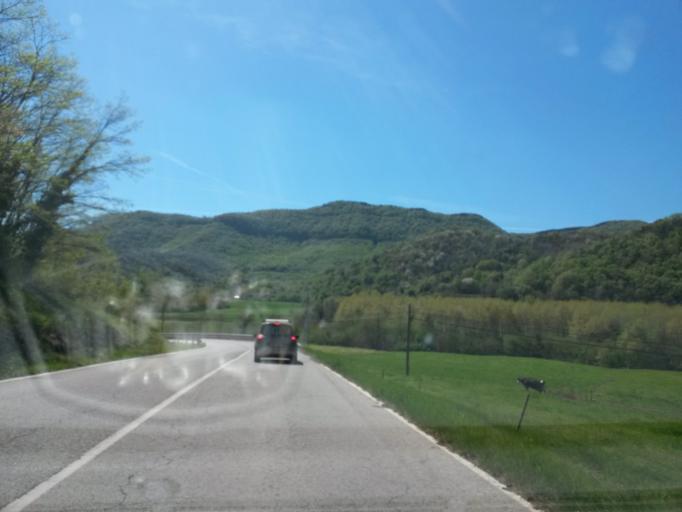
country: ES
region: Catalonia
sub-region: Provincia de Girona
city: Santa Pau
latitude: 42.1461
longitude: 2.5601
